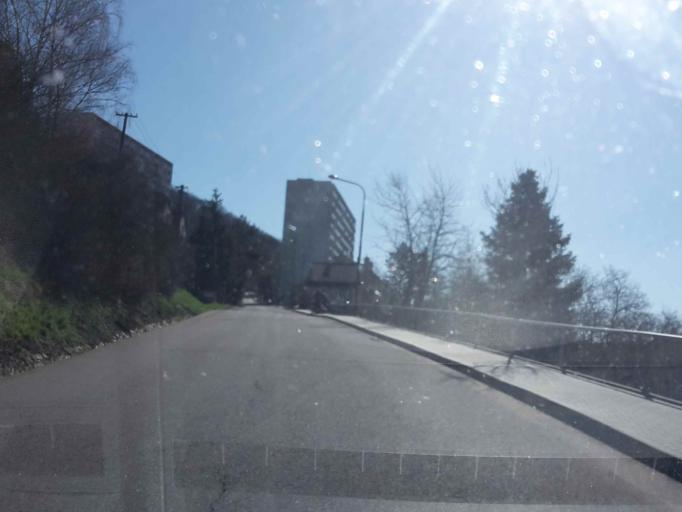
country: CZ
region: South Moravian
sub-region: Okres Blansko
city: Adamov
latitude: 49.3003
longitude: 16.6577
